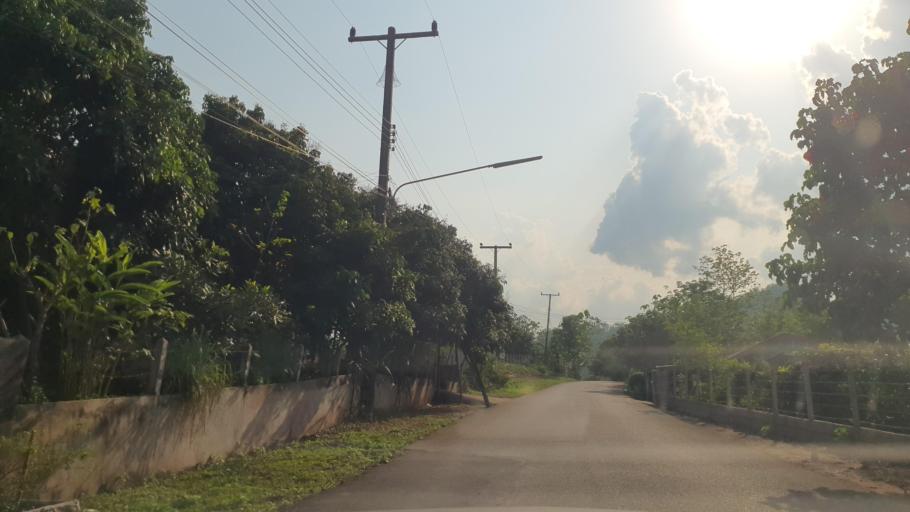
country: TH
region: Chiang Mai
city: Mae Wang
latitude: 18.6890
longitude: 98.8088
